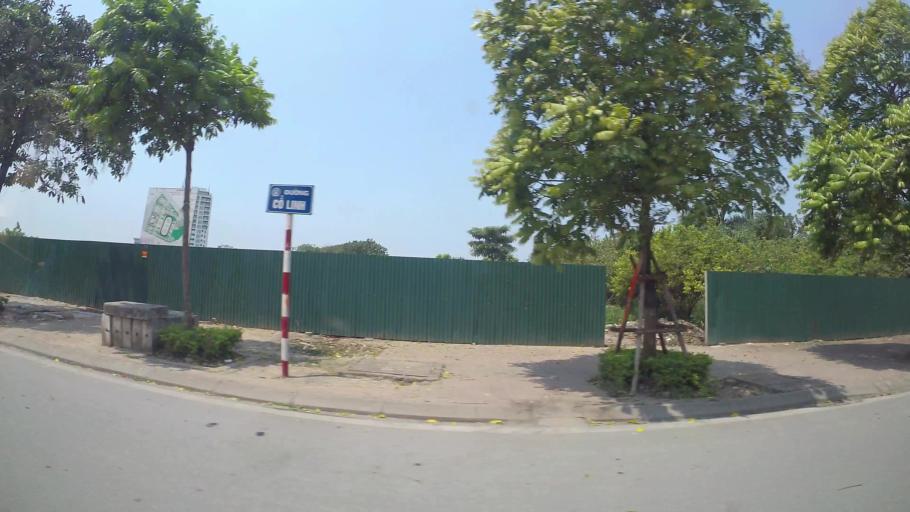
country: VN
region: Ha Noi
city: Hoan Kiem
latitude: 21.0280
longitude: 105.8935
